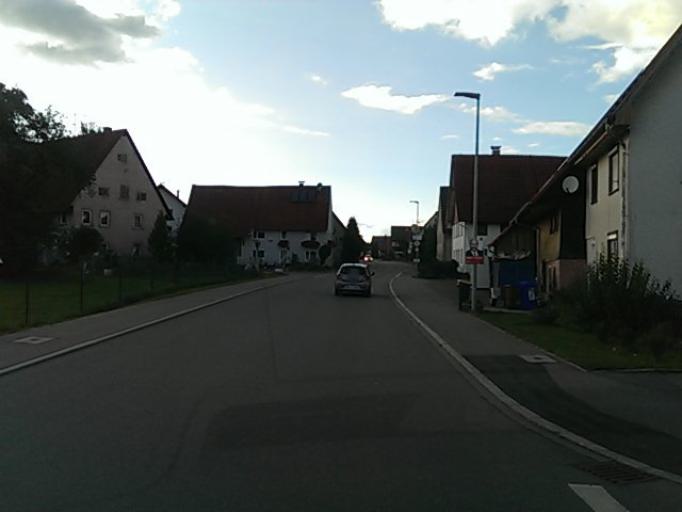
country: DE
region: Baden-Wuerttemberg
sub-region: Freiburg Region
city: Seedorf
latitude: 48.2697
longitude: 8.4851
